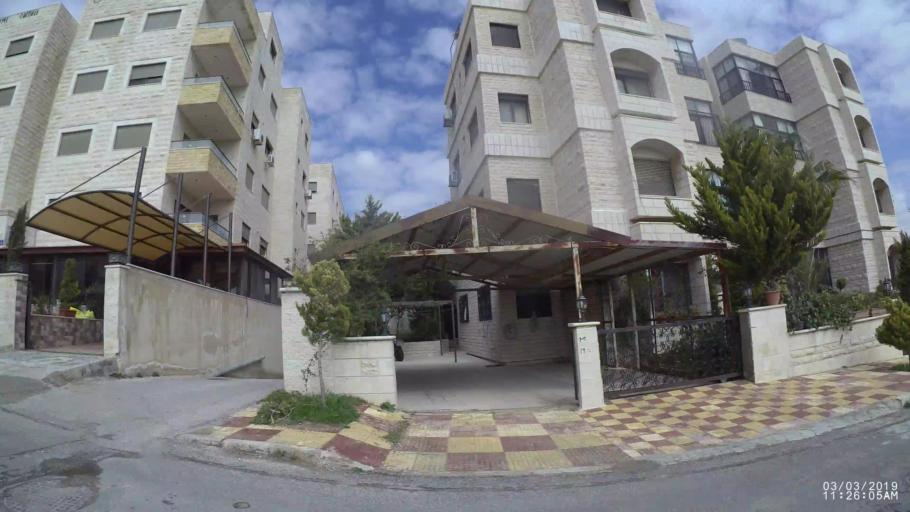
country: JO
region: Amman
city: Amman
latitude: 31.9986
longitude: 35.9167
